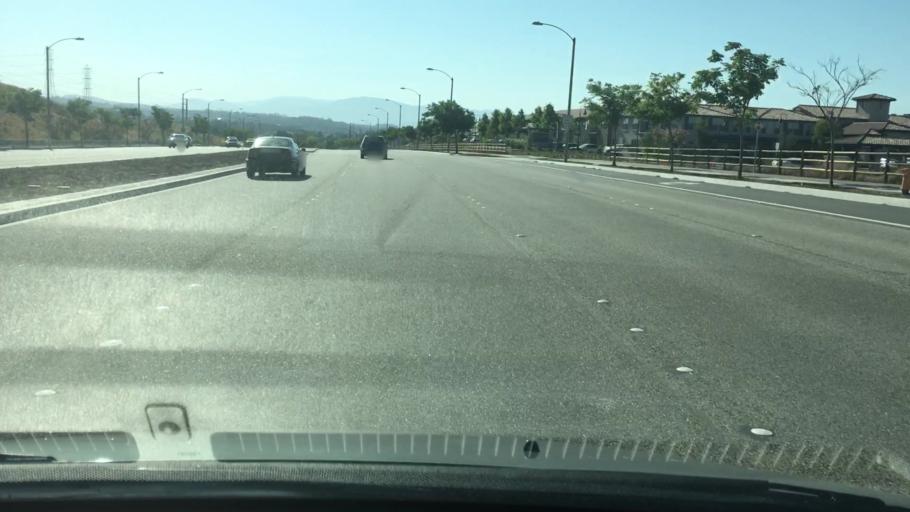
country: US
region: California
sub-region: Los Angeles County
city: Valencia
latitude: 34.4421
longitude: -118.5937
